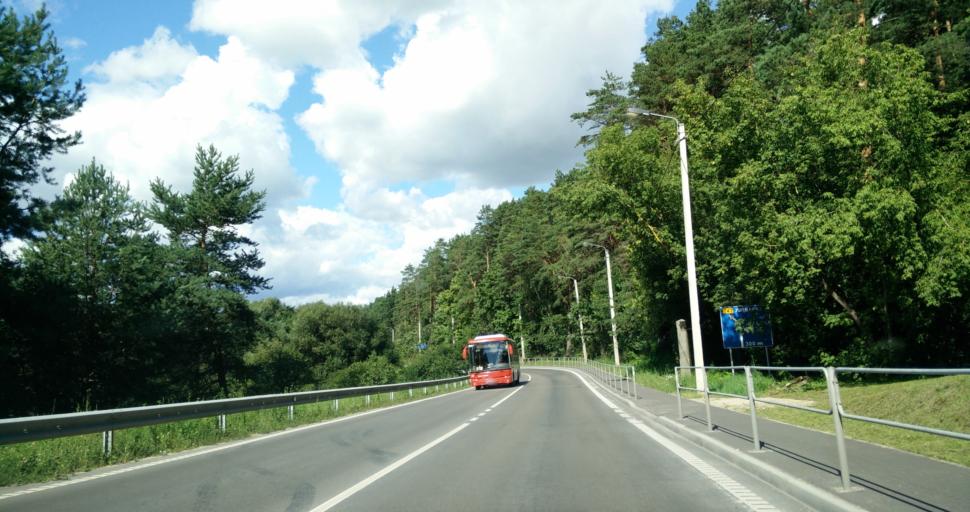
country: LT
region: Kauno apskritis
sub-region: Kauno rajonas
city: Akademija (Kaunas)
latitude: 54.9253
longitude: 23.7932
